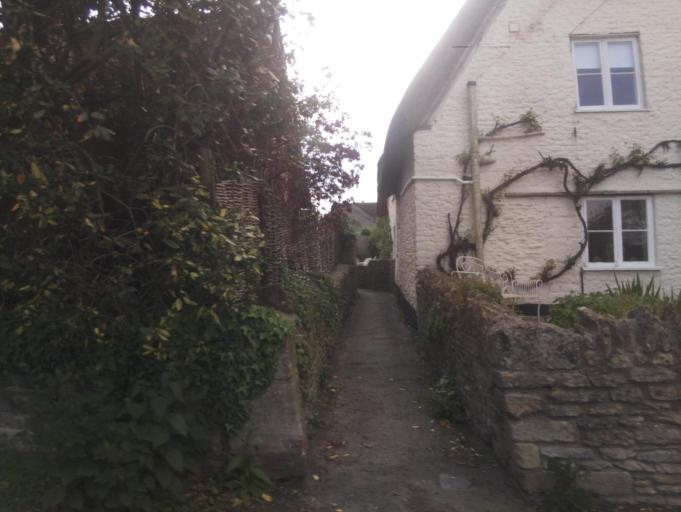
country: GB
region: England
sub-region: Wiltshire
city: Chippenham
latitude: 51.5080
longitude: -2.0783
